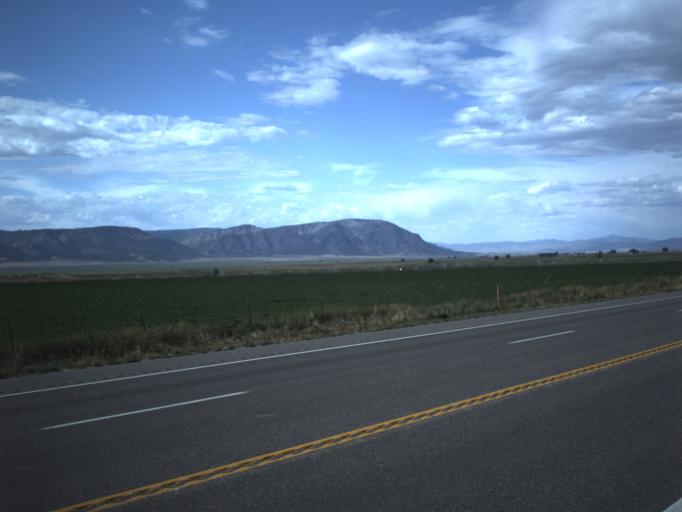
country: US
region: Utah
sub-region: Sanpete County
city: Manti
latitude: 39.2870
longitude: -111.6264
